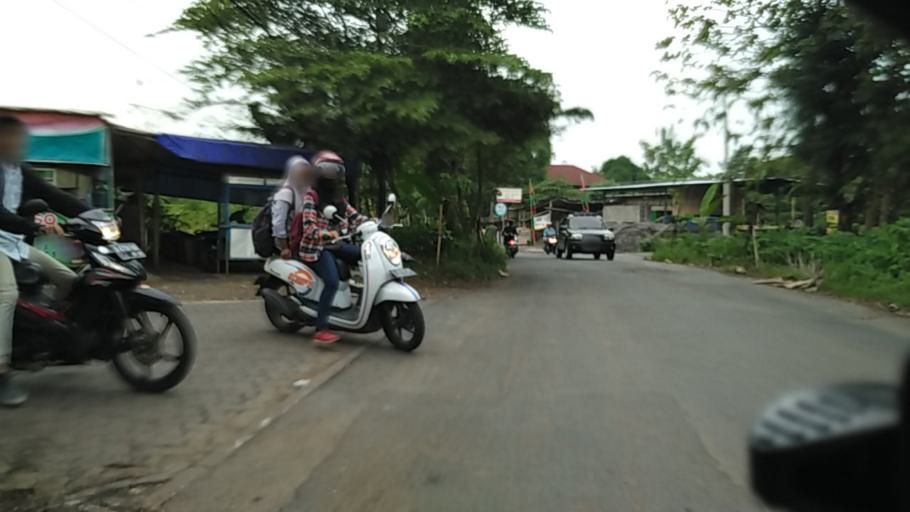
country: ID
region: Central Java
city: Semarang
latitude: -7.0675
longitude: 110.4317
